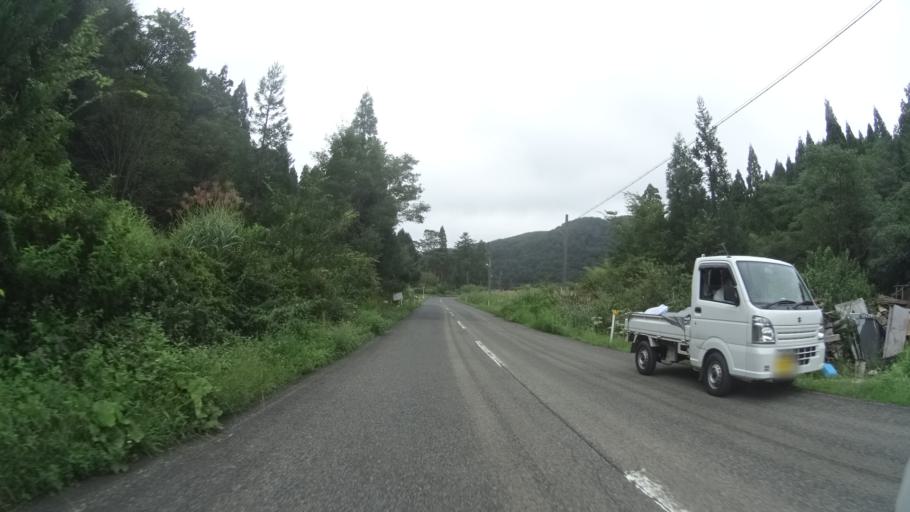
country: JP
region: Tottori
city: Kurayoshi
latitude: 35.4065
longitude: 133.9955
